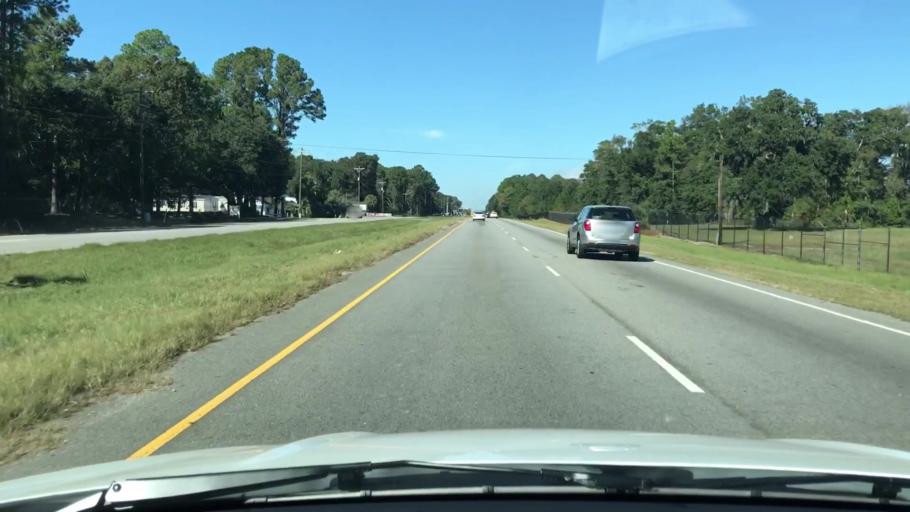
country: US
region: South Carolina
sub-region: Beaufort County
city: Burton
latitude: 32.4864
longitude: -80.7405
